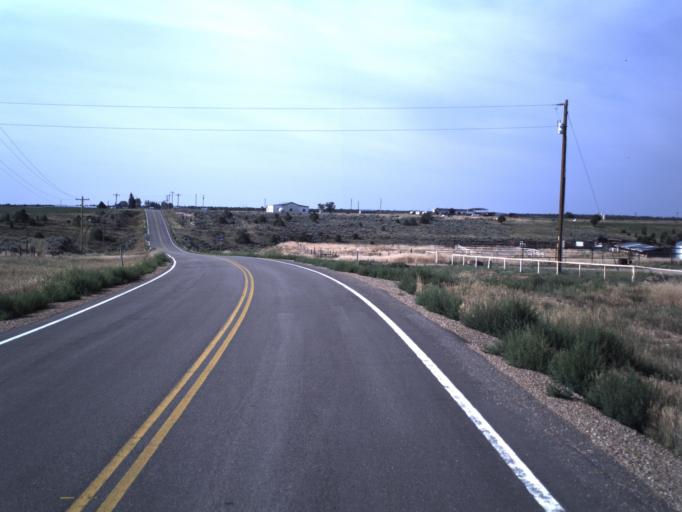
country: US
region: Utah
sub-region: Duchesne County
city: Duchesne
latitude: 40.3462
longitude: -110.4078
